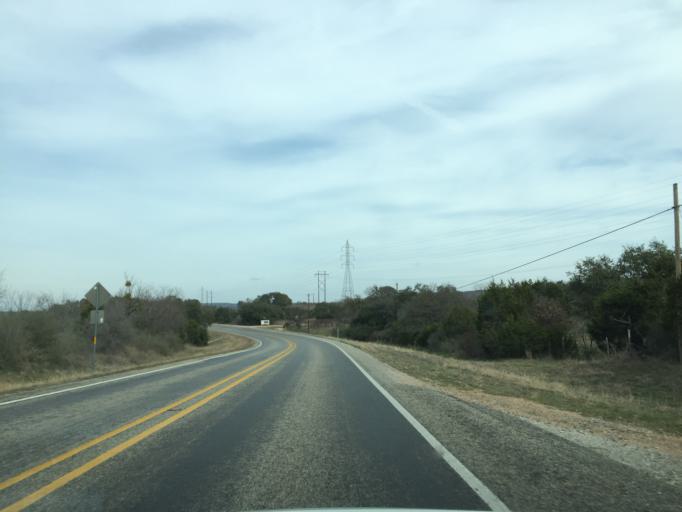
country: US
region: Texas
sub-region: Gillespie County
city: Fredericksburg
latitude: 30.4743
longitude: -98.7112
